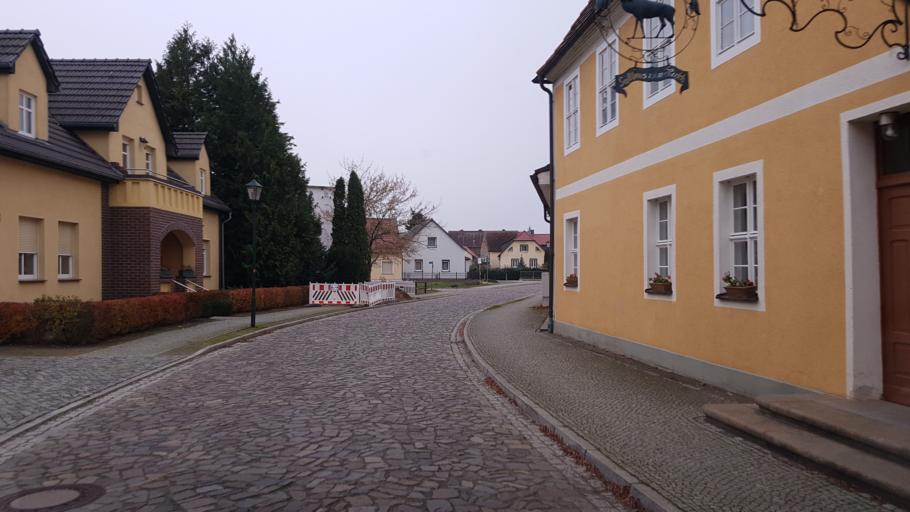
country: DE
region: Brandenburg
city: Crinitz
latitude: 51.7598
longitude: 13.8059
